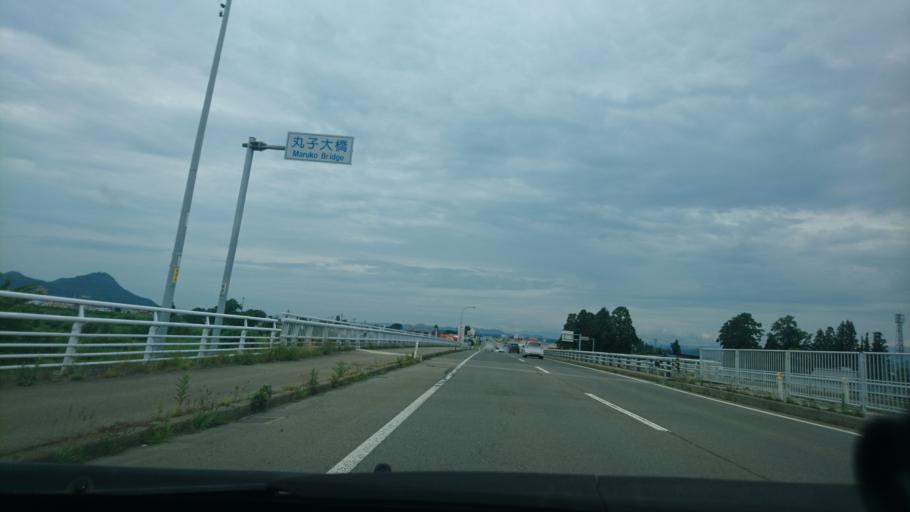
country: JP
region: Akita
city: Omagari
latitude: 39.4619
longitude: 140.4925
